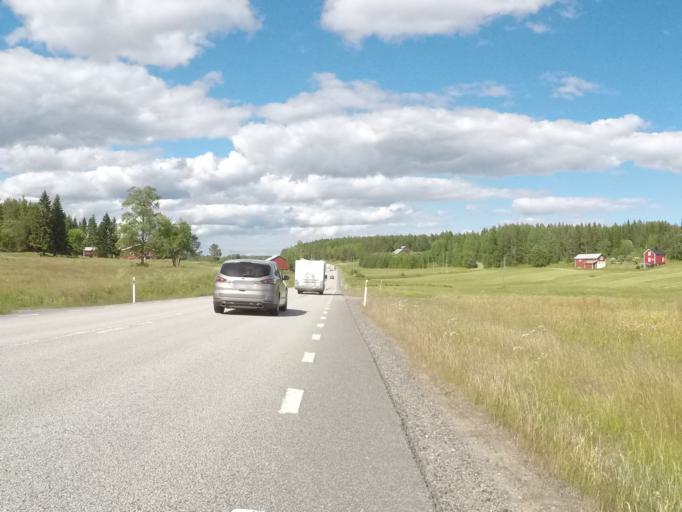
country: SE
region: Vaesterbotten
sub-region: Robertsfors Kommun
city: Robertsfors
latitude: 64.2088
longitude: 21.0173
